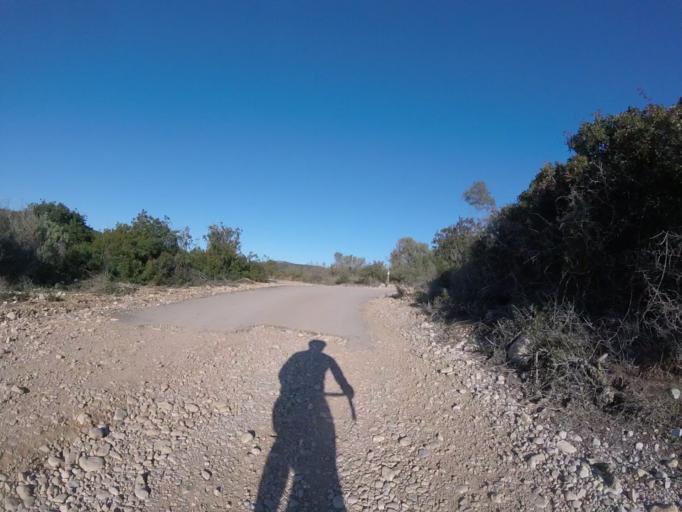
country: ES
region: Valencia
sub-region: Provincia de Castello
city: Torreblanca
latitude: 40.2642
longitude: 0.2029
